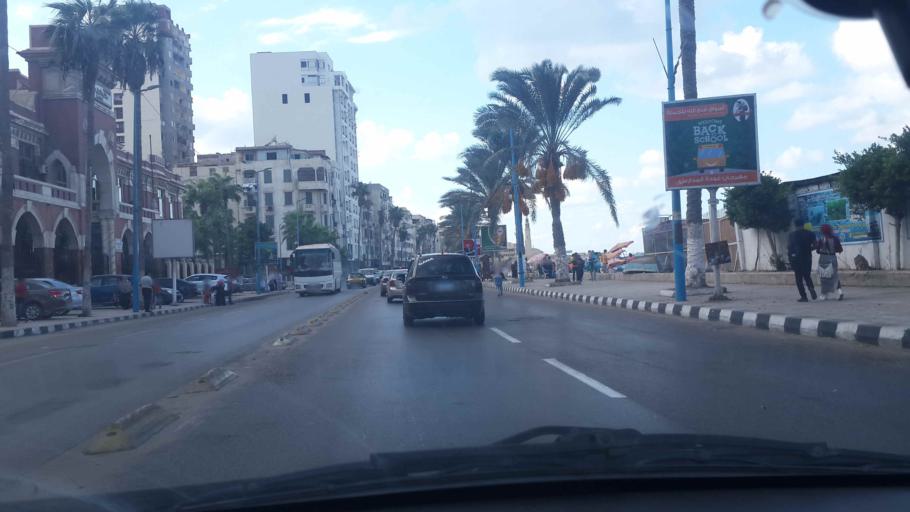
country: EG
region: Alexandria
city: Alexandria
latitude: 31.2053
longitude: 29.8845
